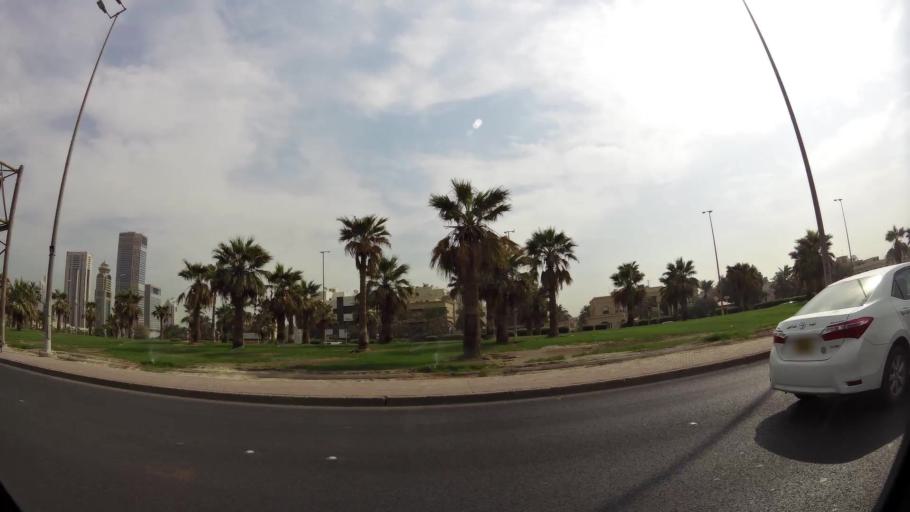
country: KW
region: Al Asimah
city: Kuwait City
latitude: 29.3567
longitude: 47.9736
